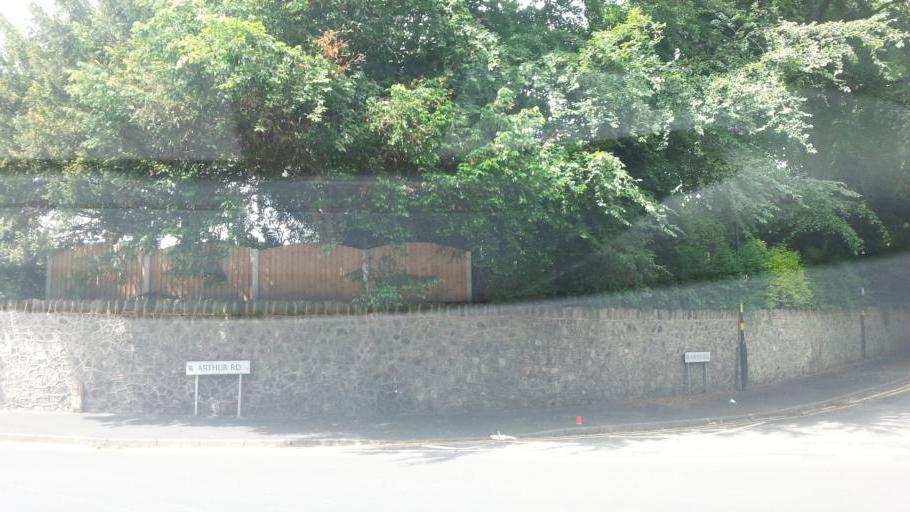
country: GB
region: England
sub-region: City and Borough of Birmingham
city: Birmingham
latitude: 52.4625
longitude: -1.9170
